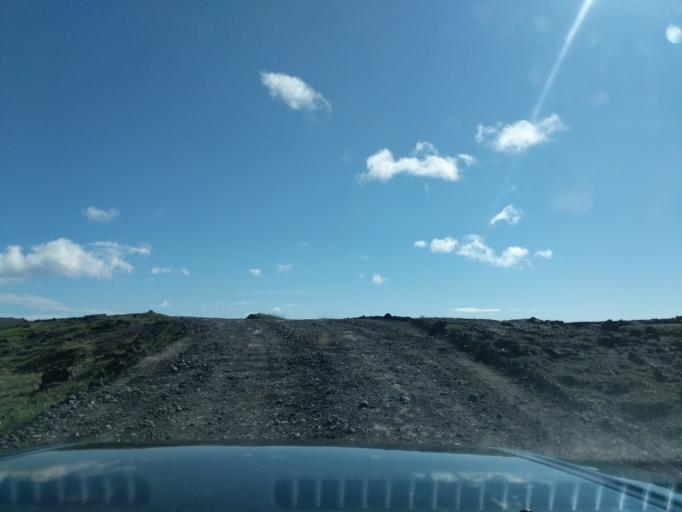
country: IS
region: West
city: Olafsvik
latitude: 64.8787
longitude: -23.9911
